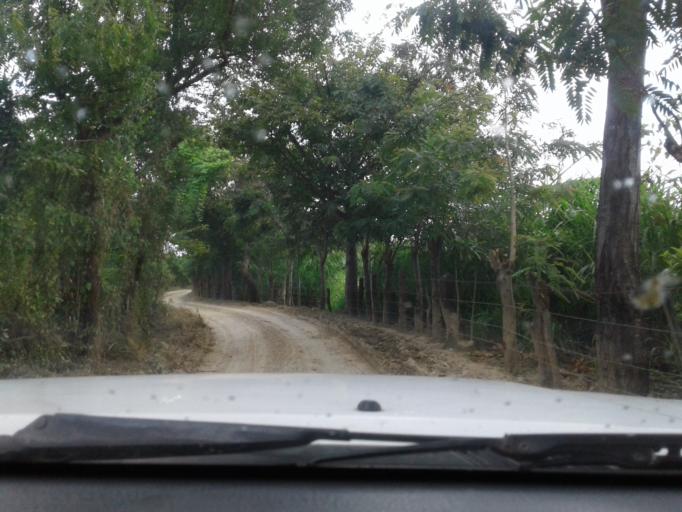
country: NI
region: Rivas
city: Belen
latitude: 11.6787
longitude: -85.8711
